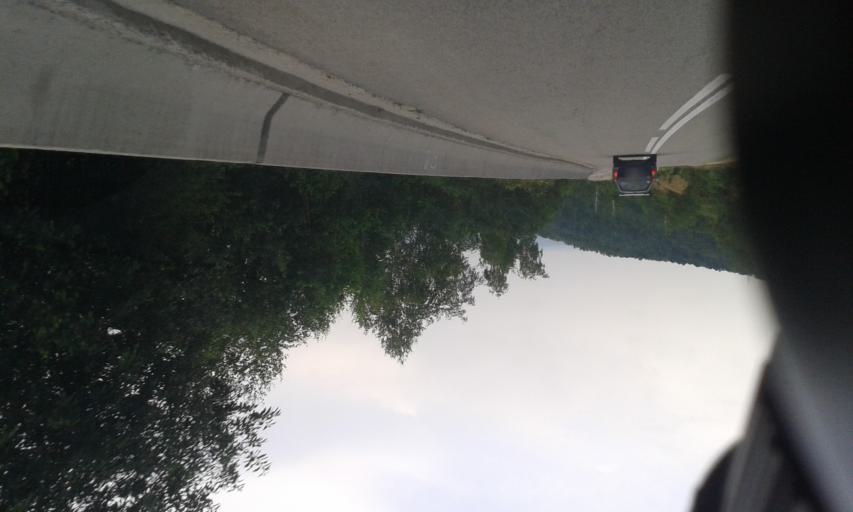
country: RO
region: Gorj
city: Novaci-Straini
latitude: 45.2144
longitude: 23.6969
